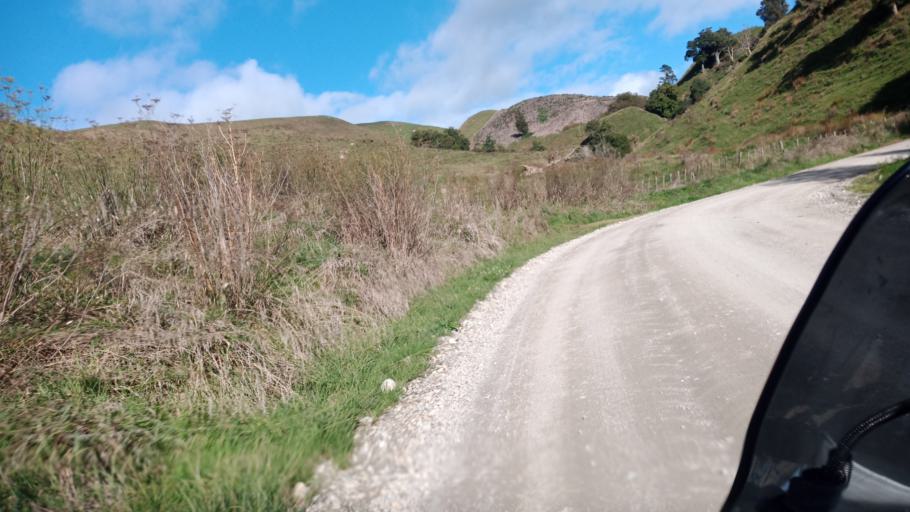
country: NZ
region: Gisborne
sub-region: Gisborne District
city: Gisborne
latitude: -38.5397
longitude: 177.5187
